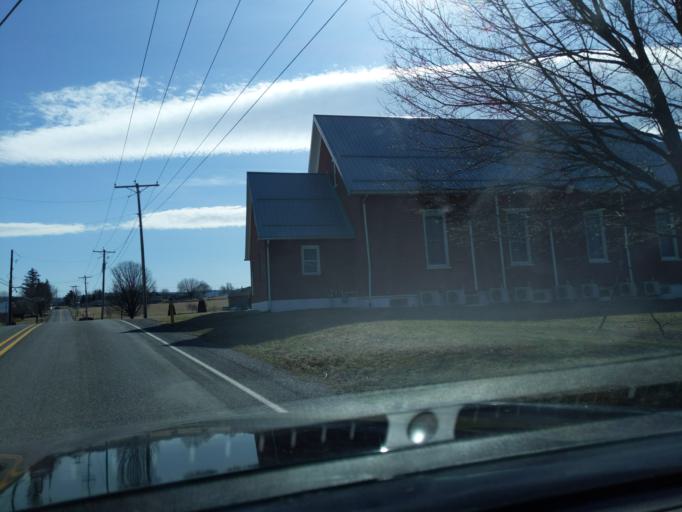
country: US
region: Pennsylvania
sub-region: Blair County
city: Martinsburg
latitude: 40.3023
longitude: -78.3341
